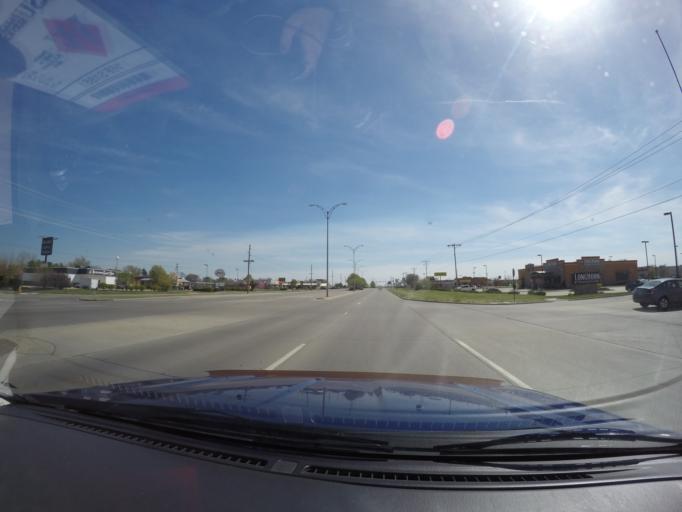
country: US
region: Kansas
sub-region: Saline County
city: Salina
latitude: 38.7940
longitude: -97.6129
